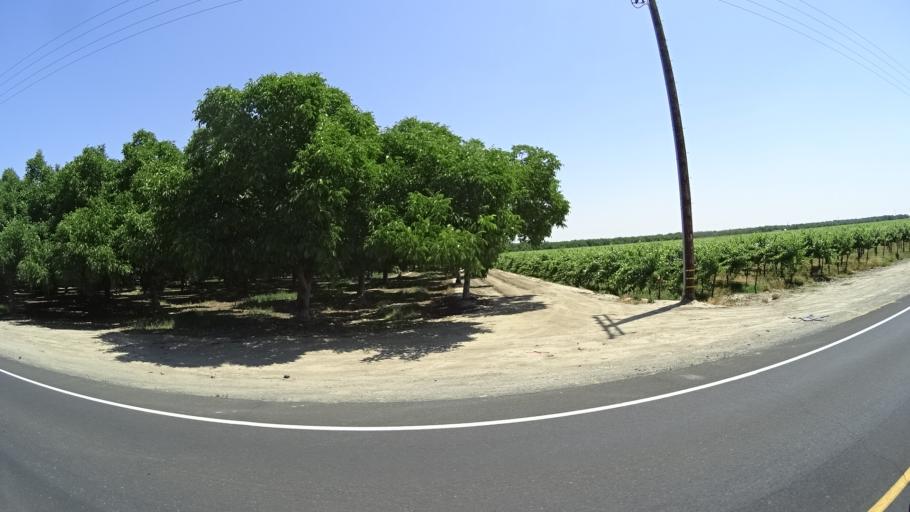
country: US
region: California
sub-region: Kings County
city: Lucerne
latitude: 36.3682
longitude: -119.6731
